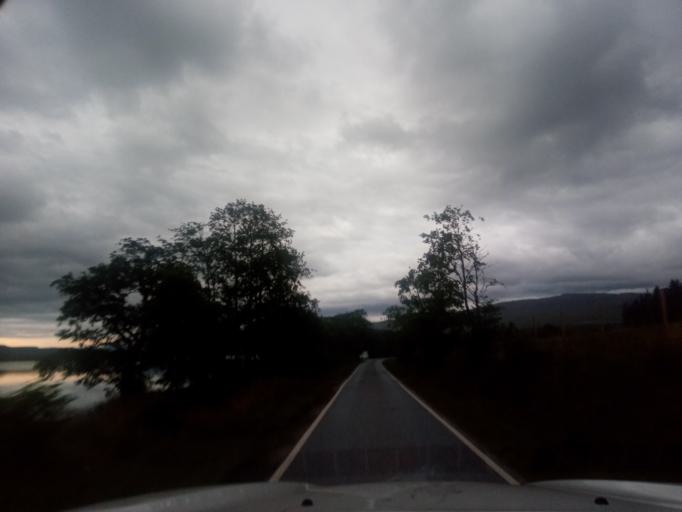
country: GB
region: Scotland
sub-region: Highland
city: Fort William
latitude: 56.8545
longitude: -5.3330
